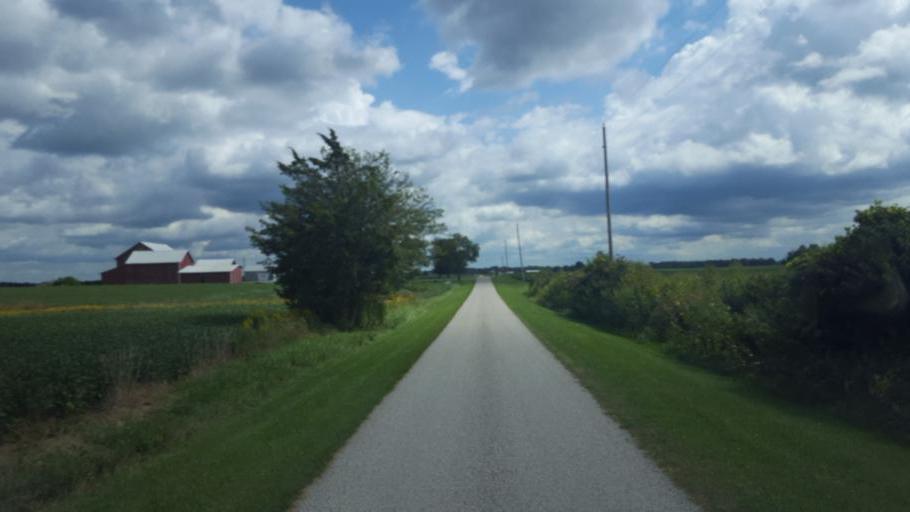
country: US
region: Ohio
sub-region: Huron County
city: Willard
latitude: 41.1159
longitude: -82.7987
